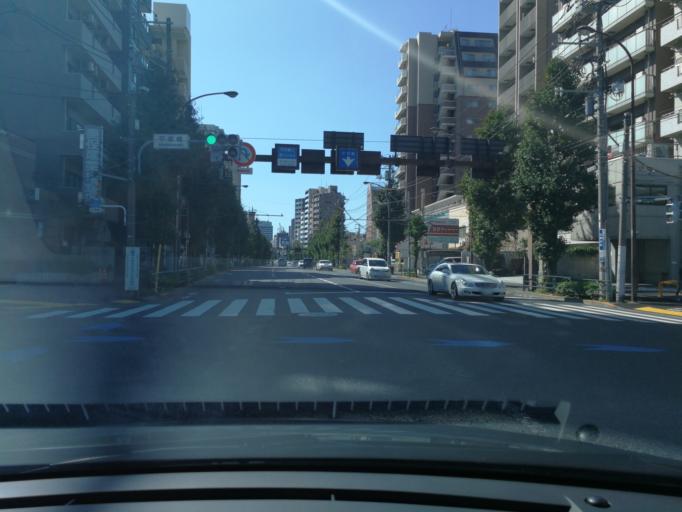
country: JP
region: Tokyo
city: Tokyo
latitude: 35.6155
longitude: 139.7090
